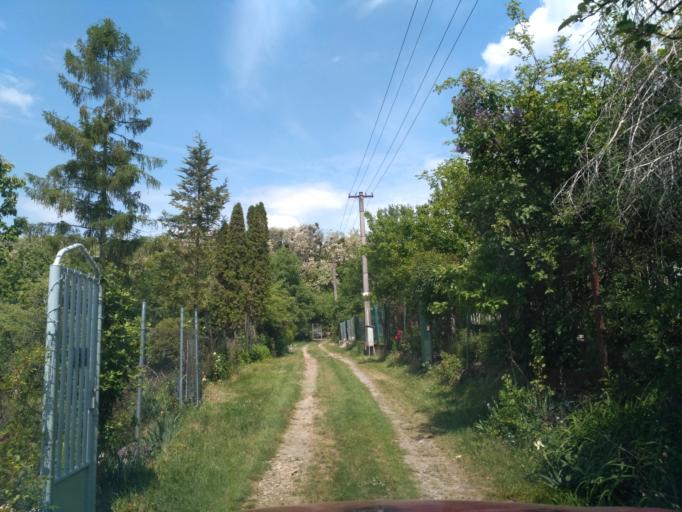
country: SK
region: Kosicky
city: Kosice
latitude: 48.7309
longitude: 21.2224
